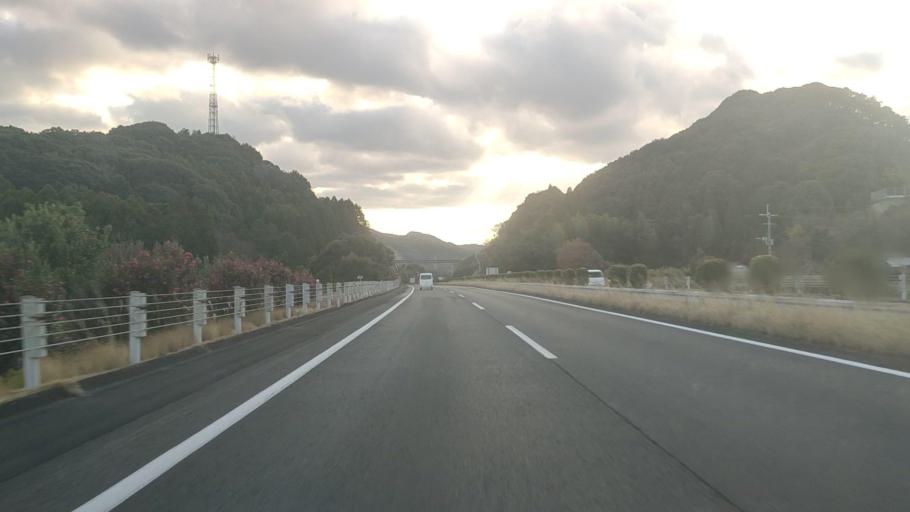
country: JP
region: Saga Prefecture
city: Takeocho-takeo
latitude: 33.2820
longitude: 130.1212
